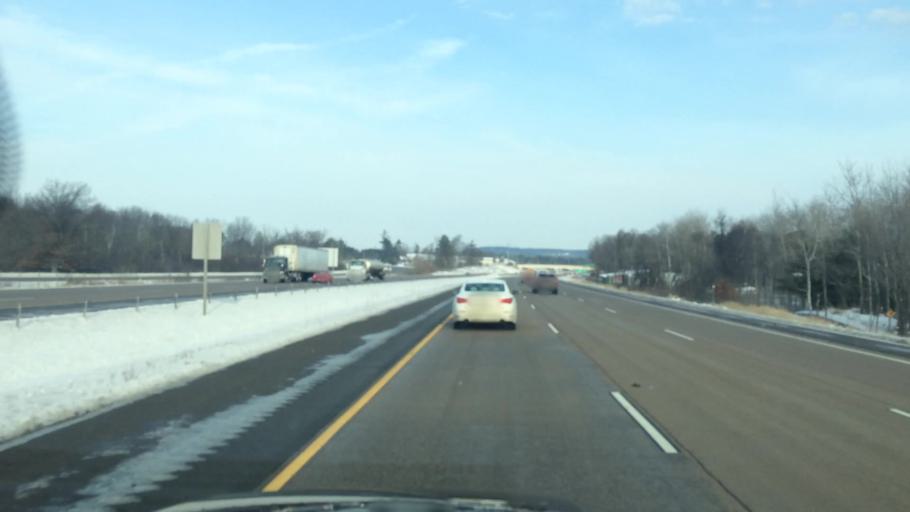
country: US
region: Wisconsin
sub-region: Marathon County
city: Rib Mountain
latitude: 44.9235
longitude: -89.6593
